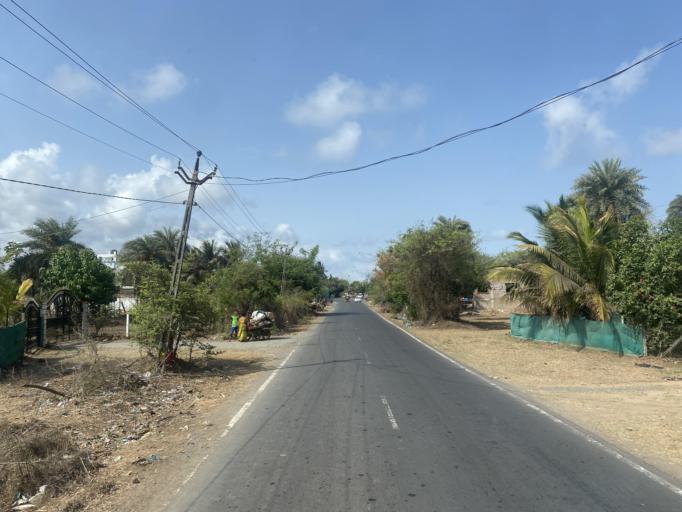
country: IN
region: Daman and Diu
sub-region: Daman District
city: Daman
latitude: 20.3382
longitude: 72.8030
